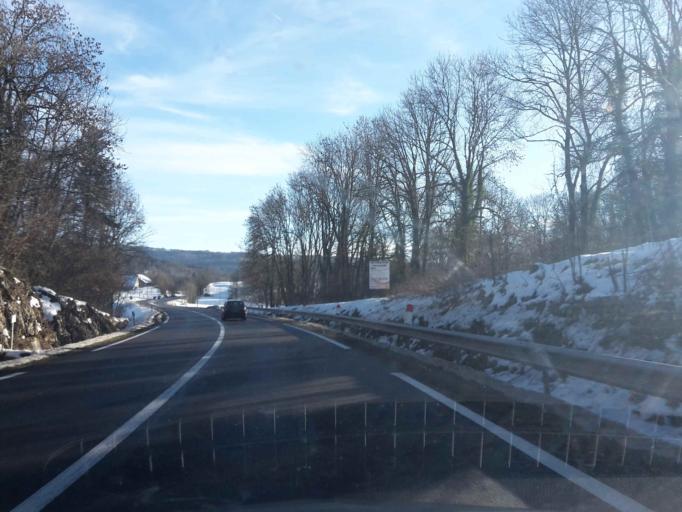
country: FR
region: Franche-Comte
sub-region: Departement du Doubs
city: Valdahon
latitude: 47.0624
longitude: 6.3458
